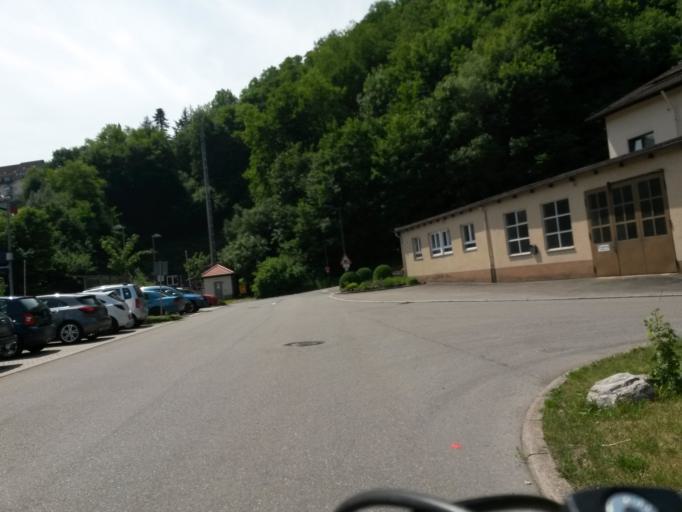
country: DE
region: Baden-Wuerttemberg
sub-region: Karlsruhe Region
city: Wildberg
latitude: 48.6253
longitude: 8.7427
